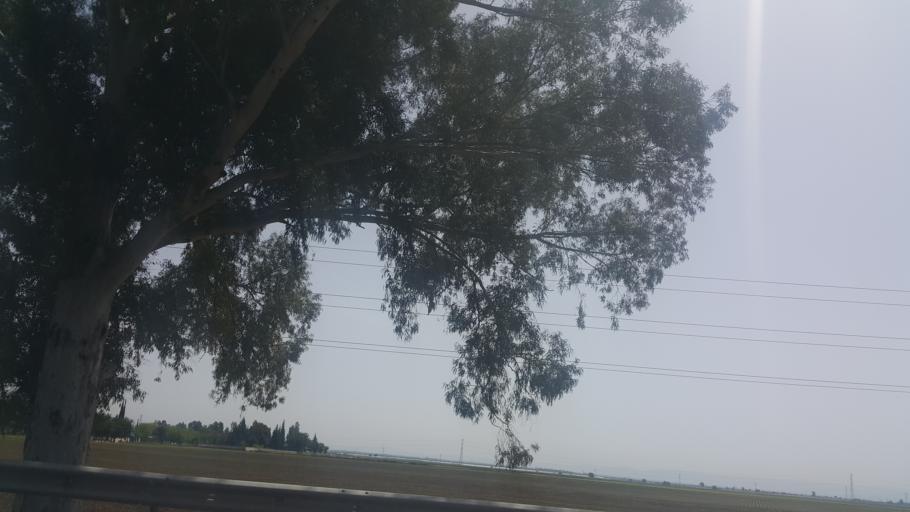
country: TR
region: Hatay
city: Serinyol
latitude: 36.3833
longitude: 36.2300
